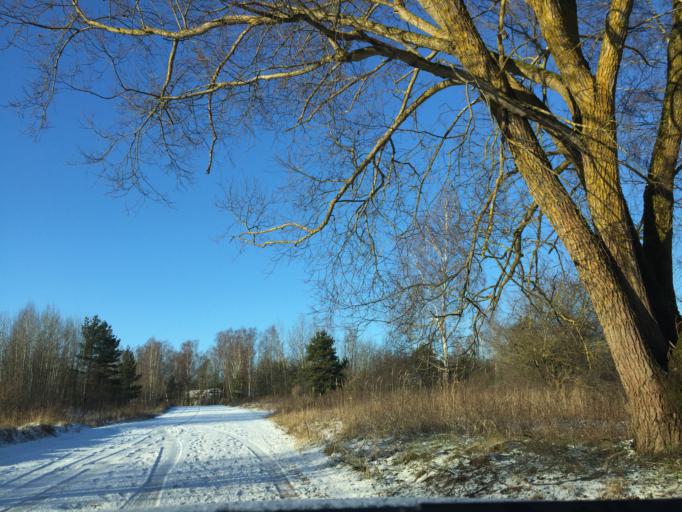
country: LV
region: Kekava
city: Balozi
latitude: 56.9088
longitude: 24.1364
